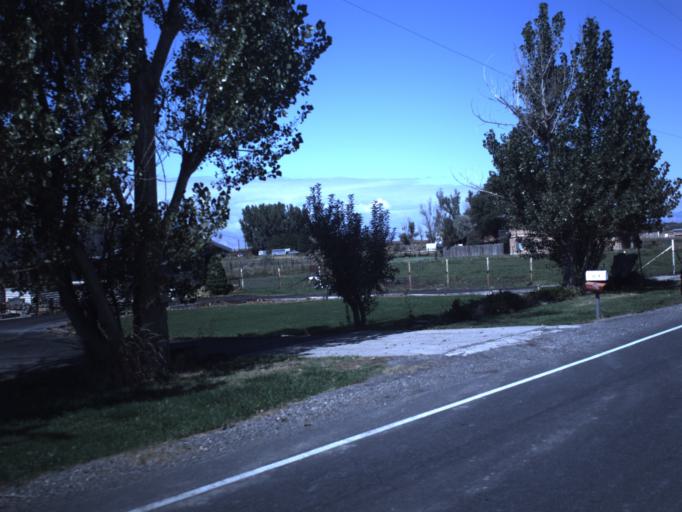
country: US
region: Utah
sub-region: Utah County
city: Benjamin
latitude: 40.1411
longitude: -111.7304
